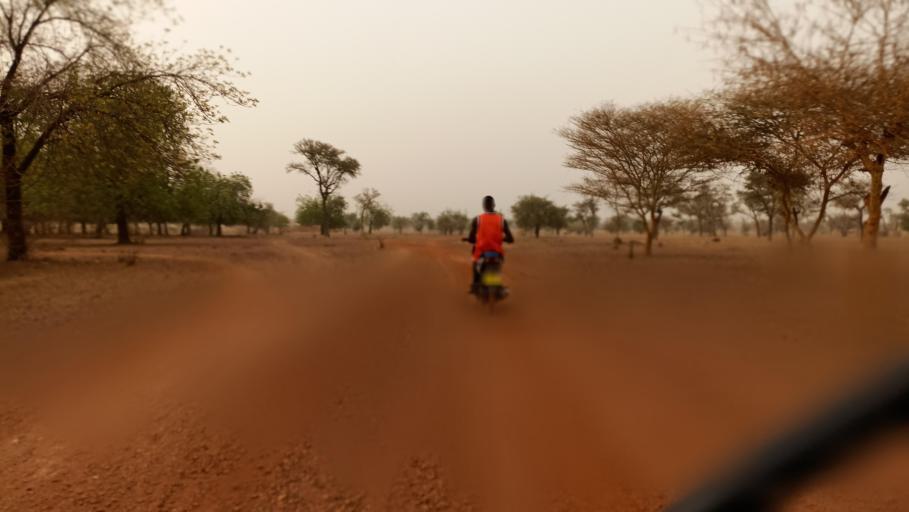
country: BF
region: Nord
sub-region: Province du Zondoma
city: Gourcy
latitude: 13.2413
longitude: -2.5849
